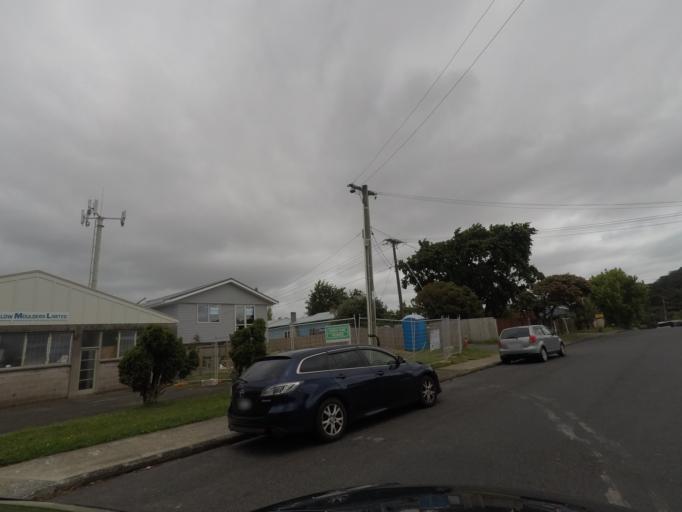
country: NZ
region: Auckland
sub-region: Auckland
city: Waitakere
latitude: -36.9078
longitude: 174.6372
